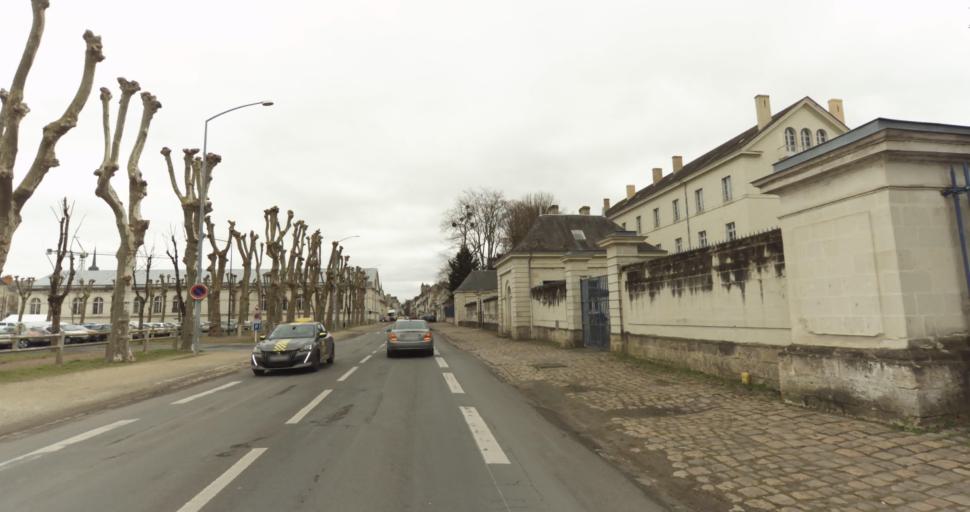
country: FR
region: Pays de la Loire
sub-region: Departement de Maine-et-Loire
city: Saumur
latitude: 47.2614
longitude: -0.0848
